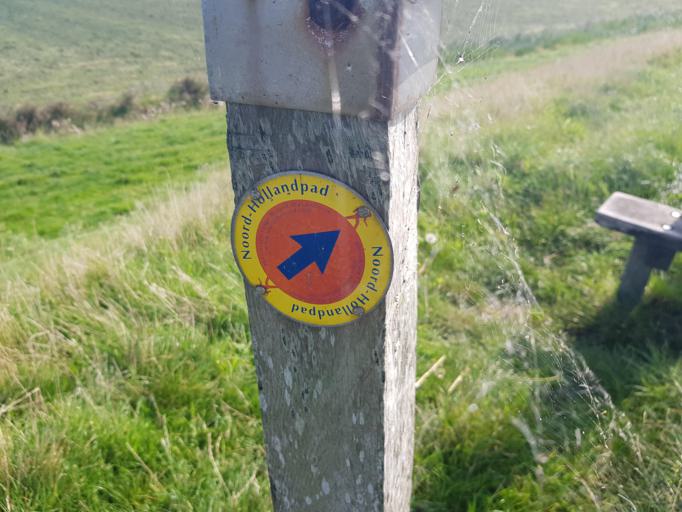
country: NL
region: North Holland
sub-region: Gemeente Texel
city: Den Burg
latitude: 53.1090
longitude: 4.8664
